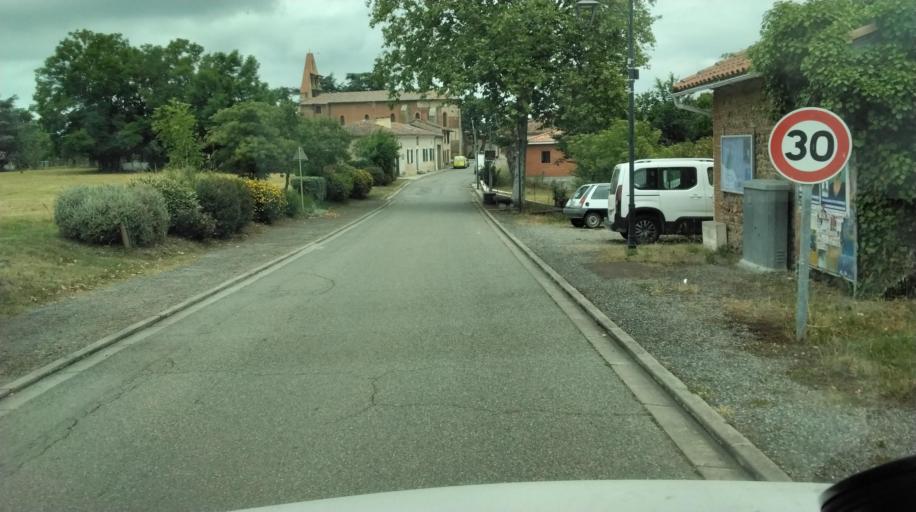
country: FR
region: Midi-Pyrenees
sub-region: Departement de la Haute-Garonne
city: Le Fousseret
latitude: 43.3053
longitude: 1.0975
